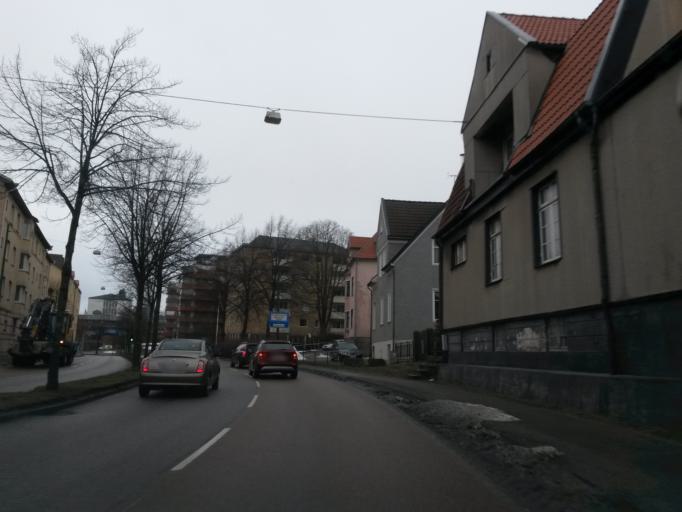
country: SE
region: Vaestra Goetaland
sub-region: Boras Kommun
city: Boras
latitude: 57.7184
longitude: 12.9466
